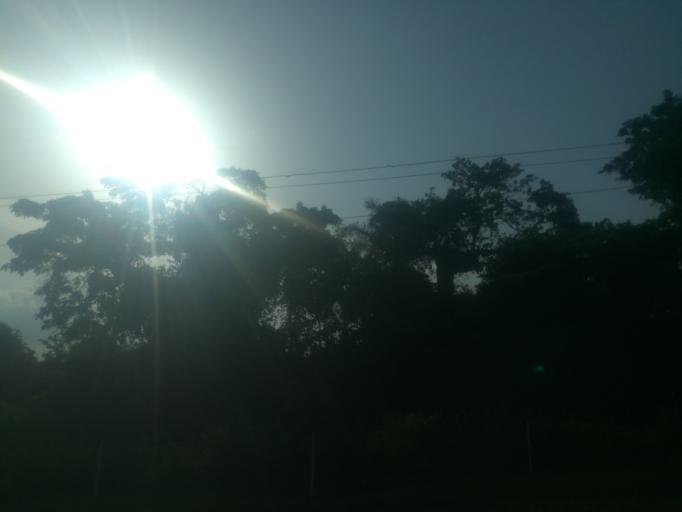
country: NG
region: Oyo
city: Moniya
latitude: 7.5033
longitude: 3.9131
